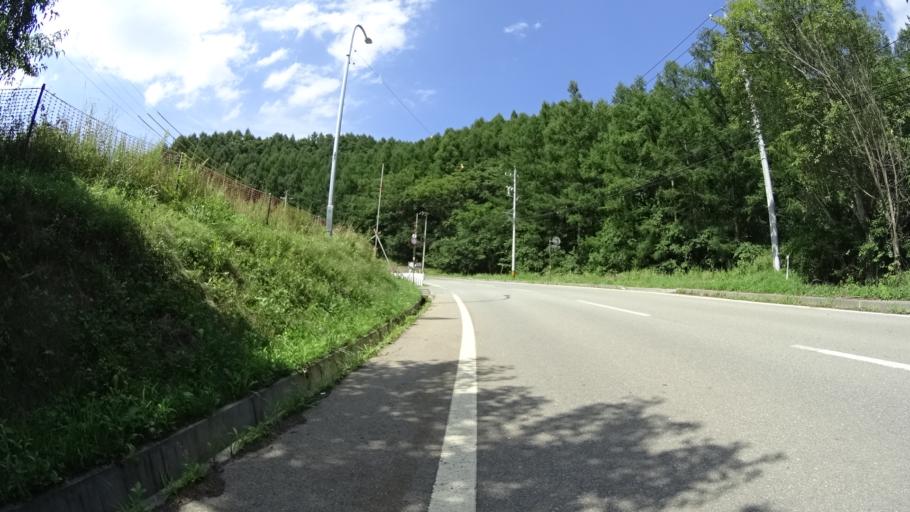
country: JP
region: Nagano
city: Saku
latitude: 36.0544
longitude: 138.4508
